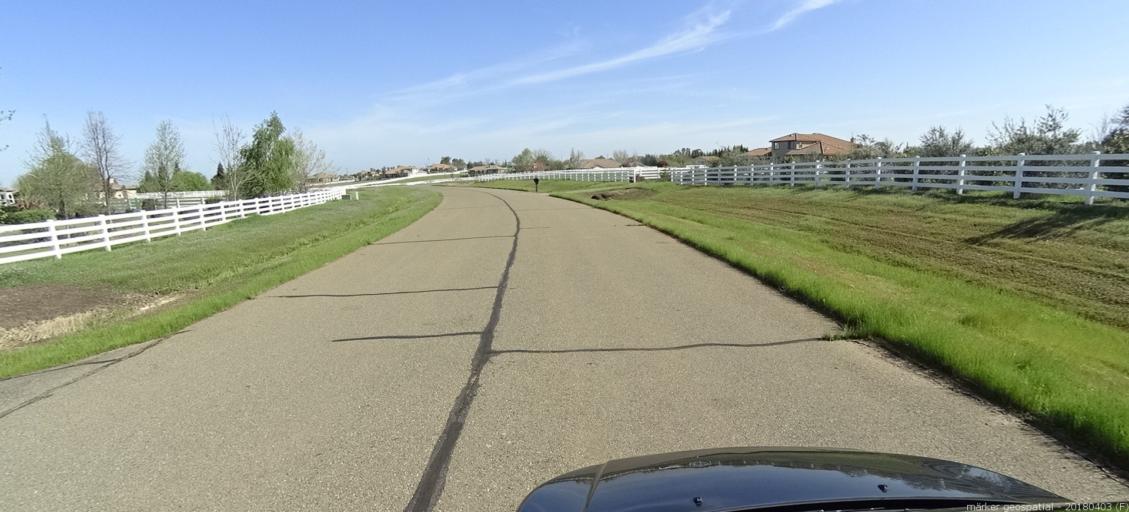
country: US
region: California
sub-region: Sacramento County
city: Wilton
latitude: 38.4173
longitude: -121.1937
